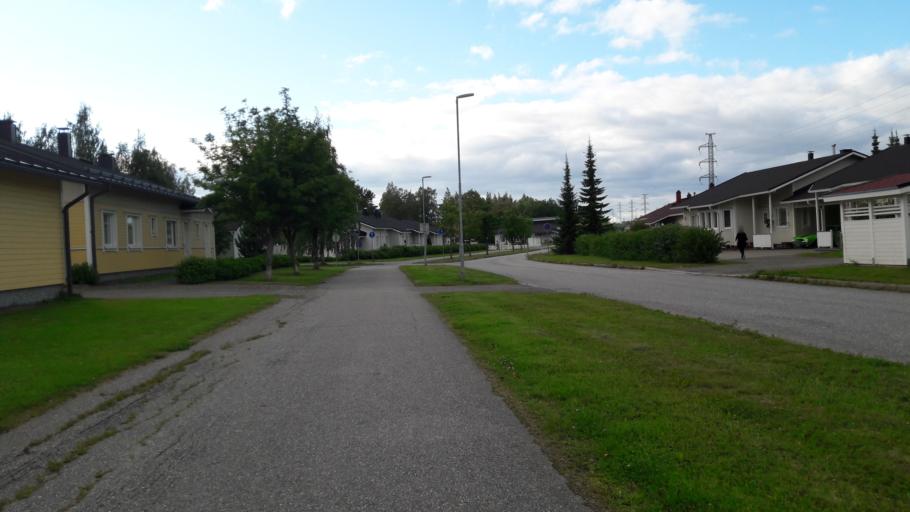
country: FI
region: North Karelia
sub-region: Joensuu
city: Joensuu
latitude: 62.5963
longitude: 29.7952
